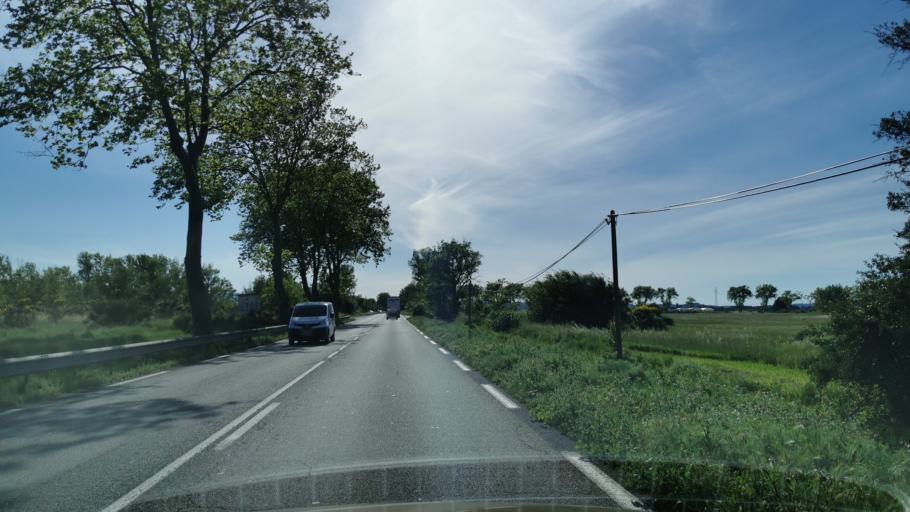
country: FR
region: Languedoc-Roussillon
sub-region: Departement de l'Aude
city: Canet
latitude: 43.2132
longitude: 2.8490
